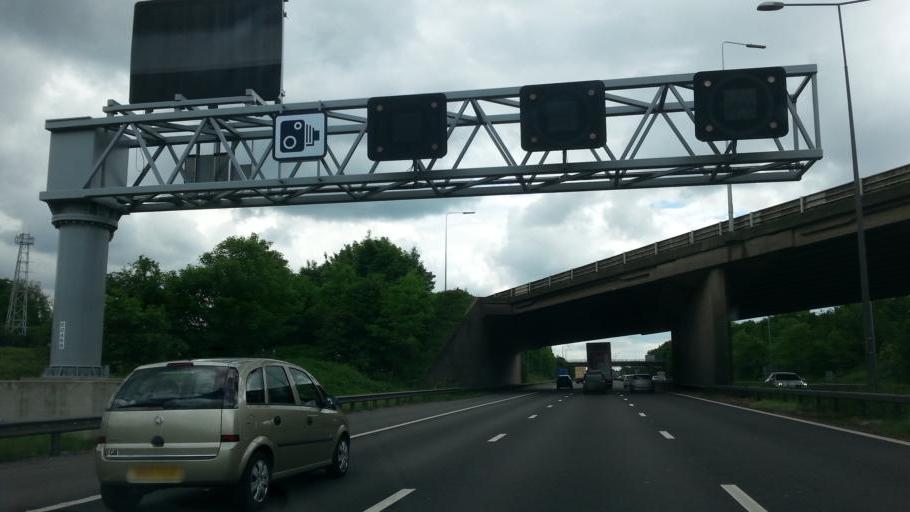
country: GB
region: England
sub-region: Staffordshire
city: Essington
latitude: 52.6374
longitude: -2.0532
